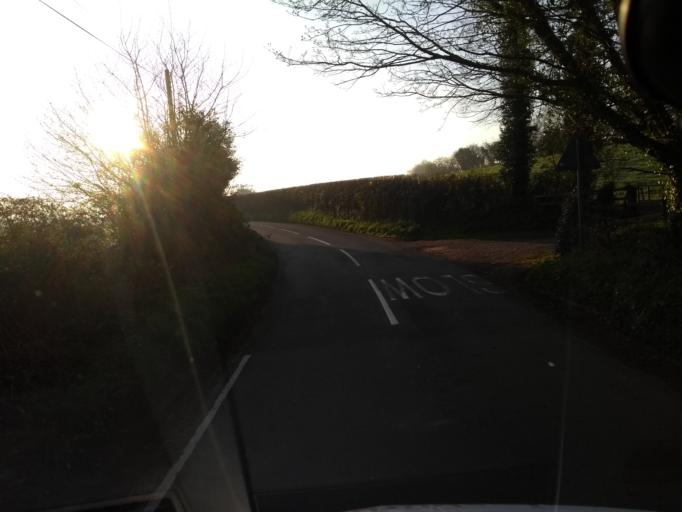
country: GB
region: England
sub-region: Somerset
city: Crewkerne
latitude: 50.8387
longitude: -2.8702
